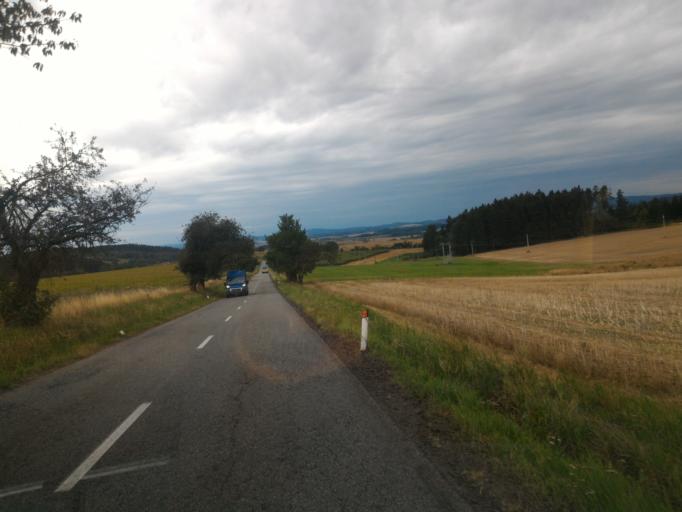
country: CZ
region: Vysocina
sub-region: Okres Jihlava
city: Trest'
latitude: 49.2363
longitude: 15.5525
